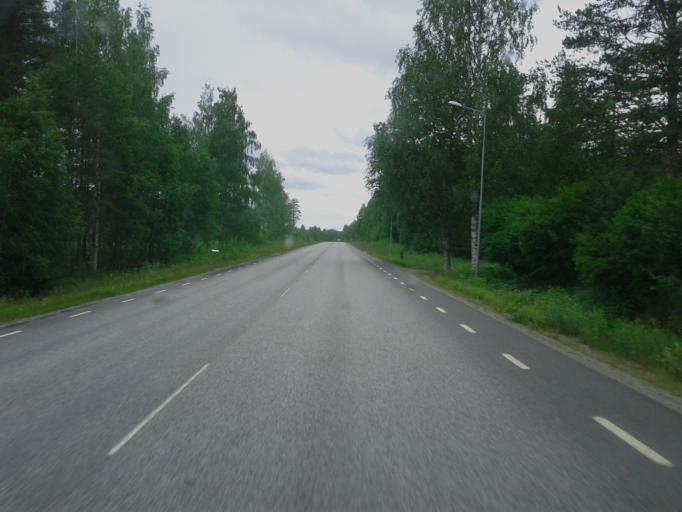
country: SE
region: Vaesterbotten
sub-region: Skelleftea Kommun
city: Langsele
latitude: 64.9177
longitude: 20.0939
